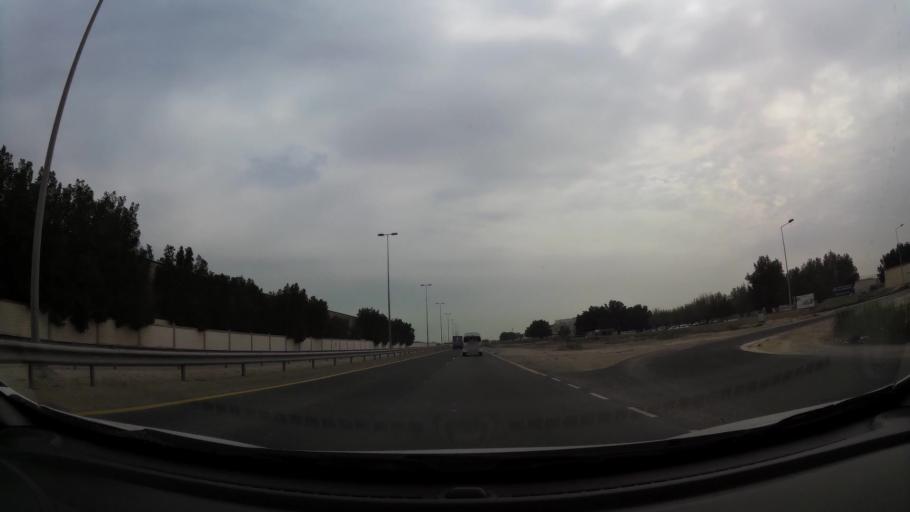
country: BH
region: Northern
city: Sitrah
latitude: 26.0816
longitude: 50.6129
